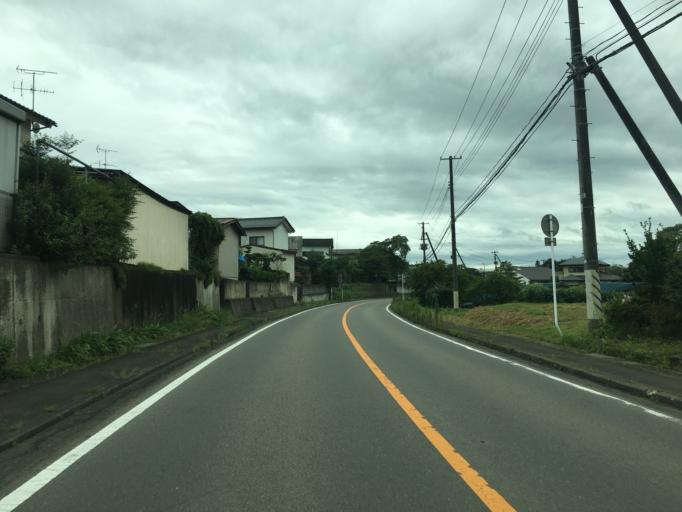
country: JP
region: Fukushima
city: Fukushima-shi
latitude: 37.6596
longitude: 140.5443
